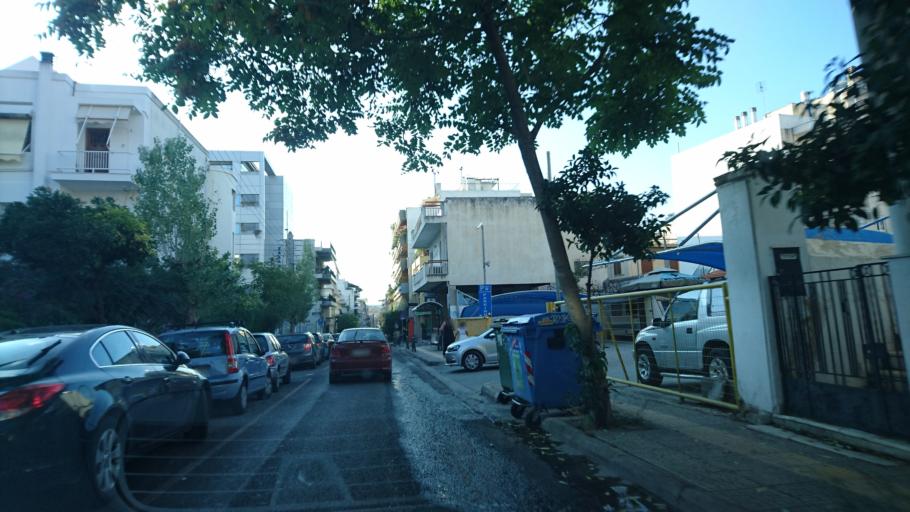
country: GR
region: Attica
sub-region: Nomarchia Athinas
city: Khalandrion
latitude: 38.0208
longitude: 23.8040
